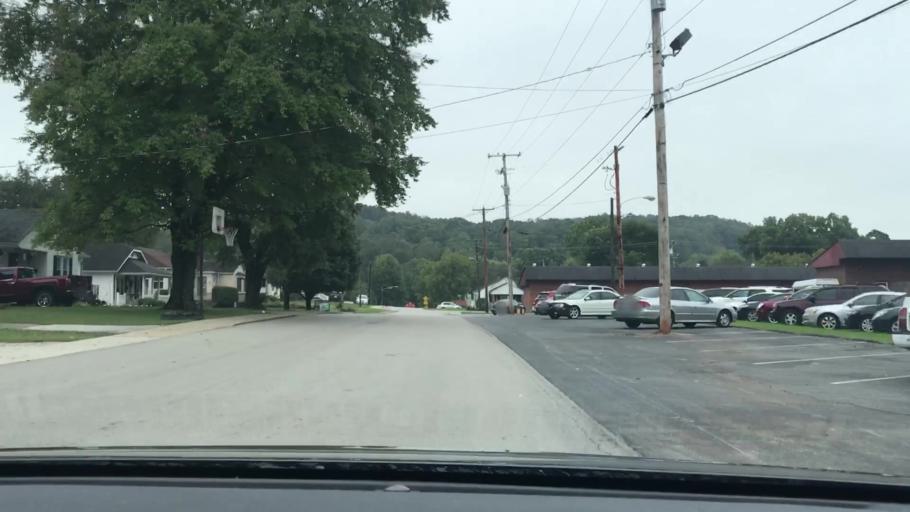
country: US
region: Kentucky
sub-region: Pulaski County
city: Somerset
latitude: 37.0863
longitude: -84.5981
